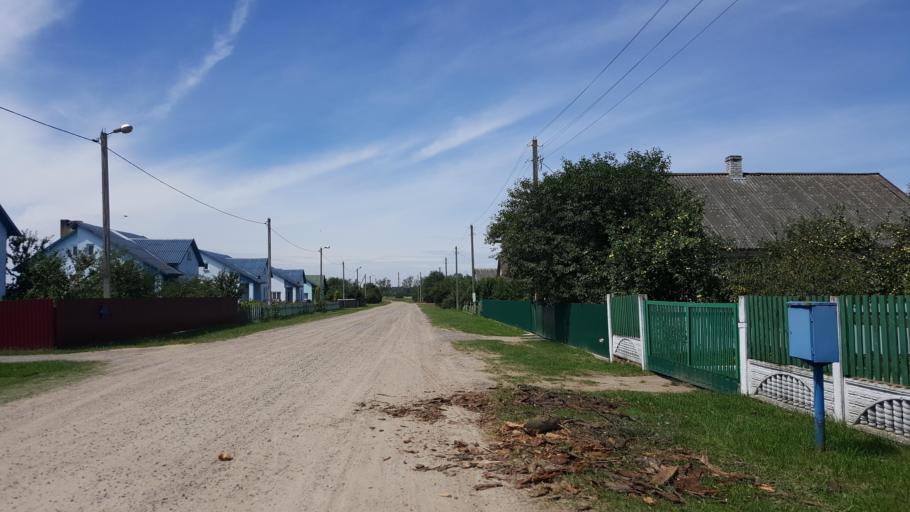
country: BY
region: Brest
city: Pruzhany
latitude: 52.5527
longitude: 24.2043
